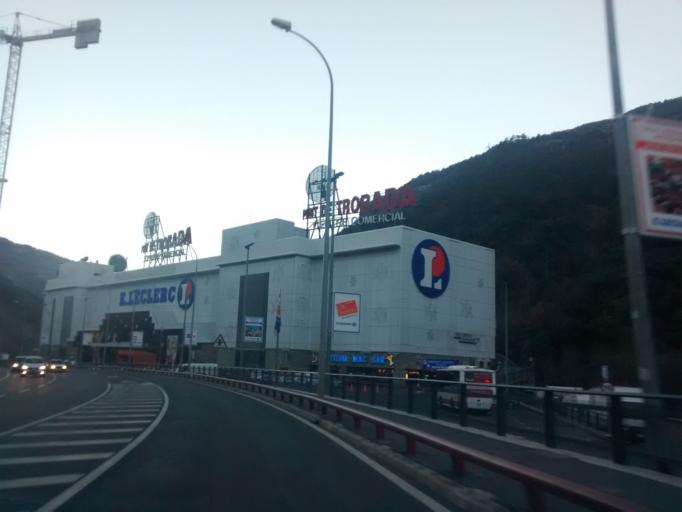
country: AD
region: Sant Julia de Loria
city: Sant Julia de Loria
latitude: 42.4485
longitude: 1.4825
